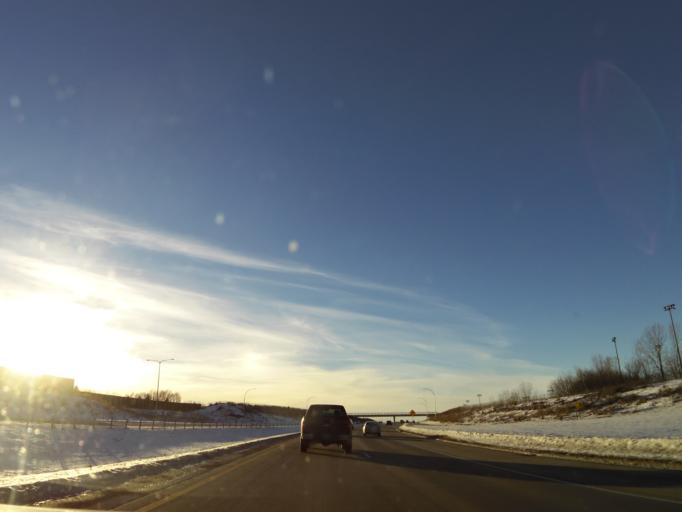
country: US
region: Minnesota
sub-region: Hennepin County
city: Eden Prairie
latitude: 44.8504
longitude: -93.4882
